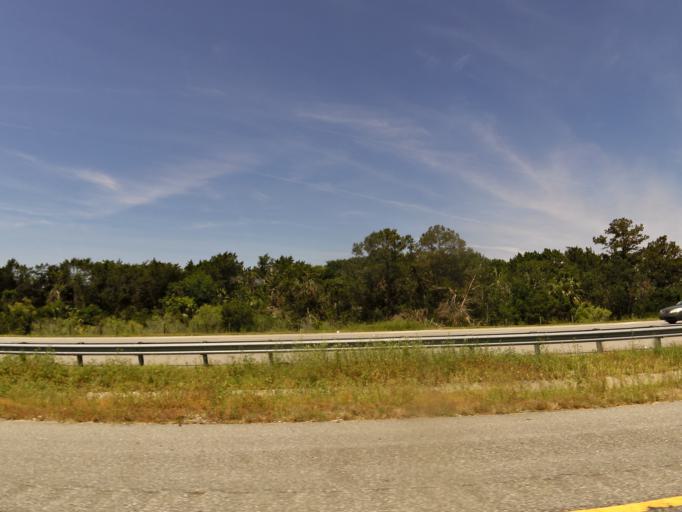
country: US
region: Georgia
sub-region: Glynn County
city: Dock Junction
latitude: 31.2058
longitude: -81.5348
